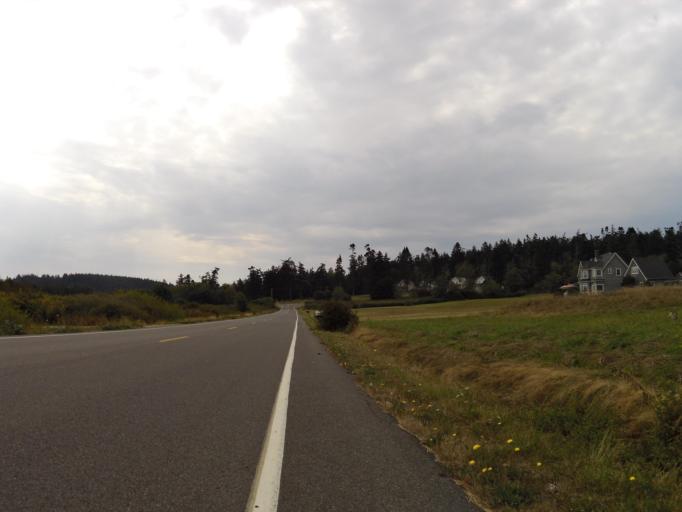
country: US
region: Washington
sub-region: Island County
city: Coupeville
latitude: 48.1719
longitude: -122.6752
